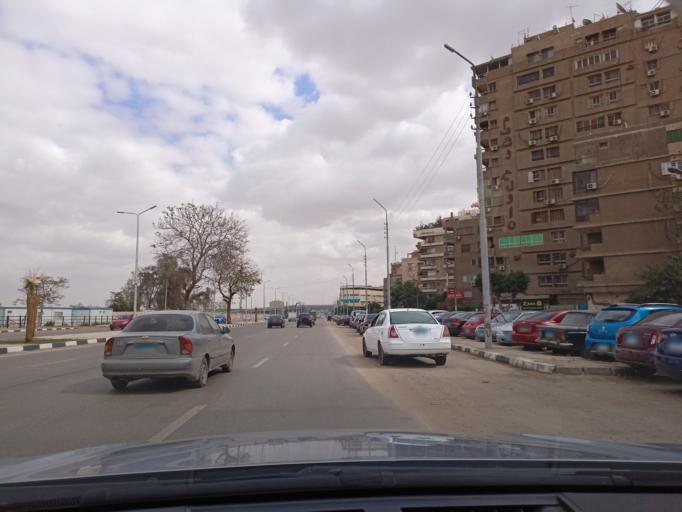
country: EG
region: Muhafazat al Qalyubiyah
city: Al Khankah
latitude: 30.1195
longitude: 31.3521
